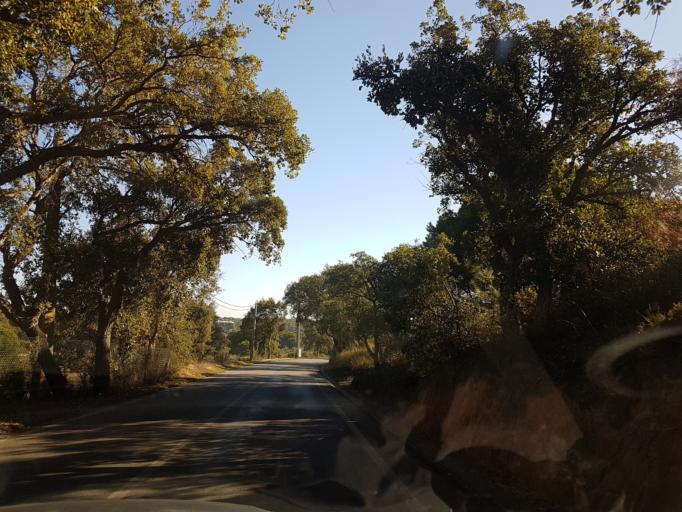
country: PT
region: Faro
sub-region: Lagoa
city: Carvoeiro
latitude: 37.1068
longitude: -8.4331
